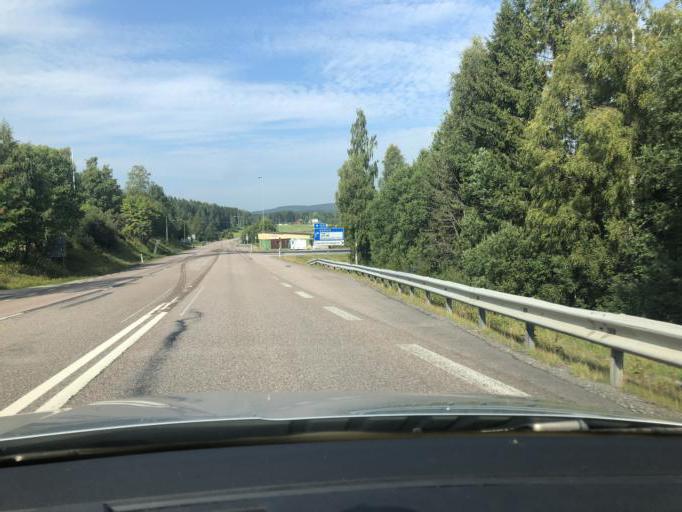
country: SE
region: Vaesternorrland
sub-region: Kramfors Kommun
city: Kramfors
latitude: 62.8178
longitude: 17.8575
